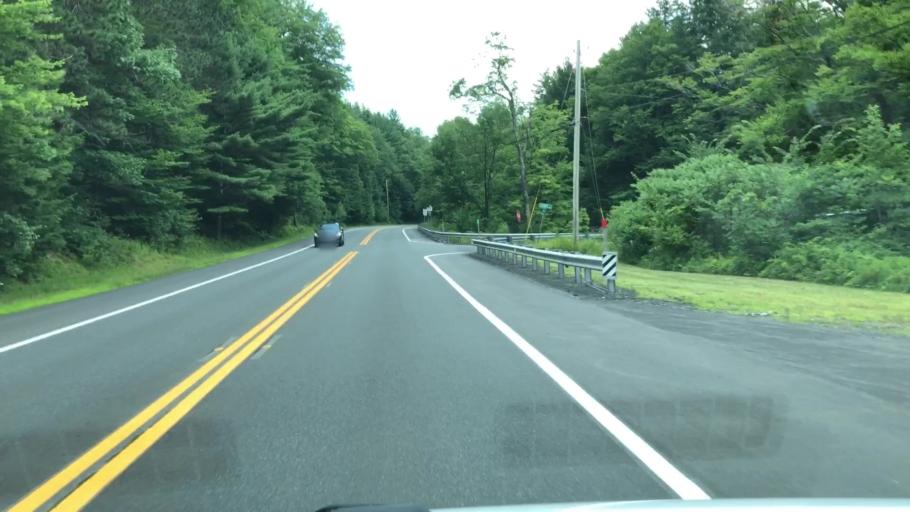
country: US
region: Massachusetts
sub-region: Hampshire County
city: Chesterfield
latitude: 42.4557
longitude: -72.8405
